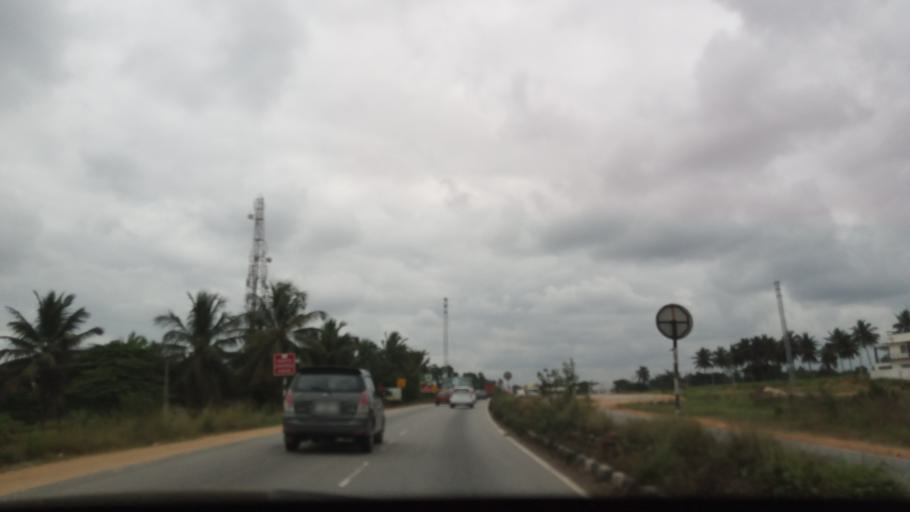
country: IN
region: Karnataka
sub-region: Mandya
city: Shrirangapattana
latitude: 12.3958
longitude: 76.6686
